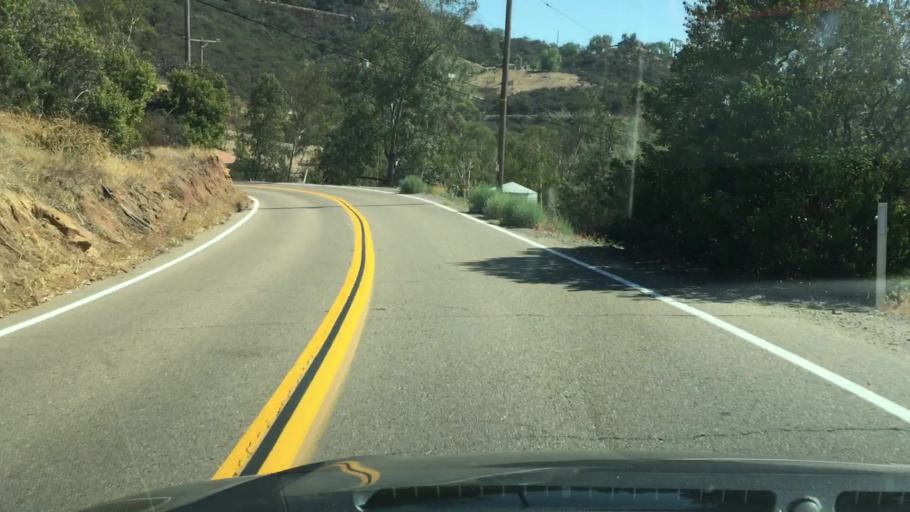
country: US
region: California
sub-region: San Diego County
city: Jamul
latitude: 32.7382
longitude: -116.8166
